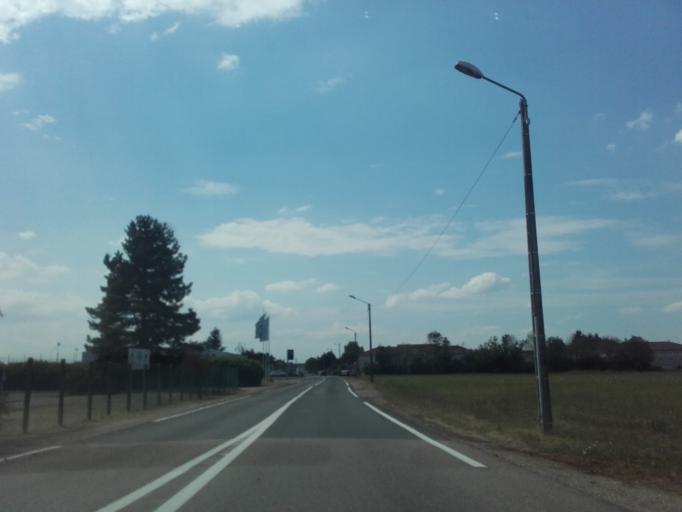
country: FR
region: Rhone-Alpes
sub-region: Departement de l'Ain
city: Loyettes
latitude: 45.7806
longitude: 5.2151
